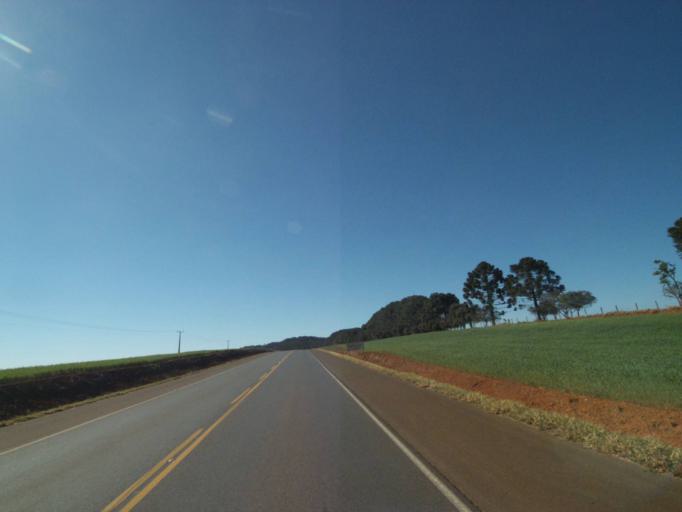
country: BR
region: Parana
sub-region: Tibagi
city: Tibagi
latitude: -24.4204
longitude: -50.3716
